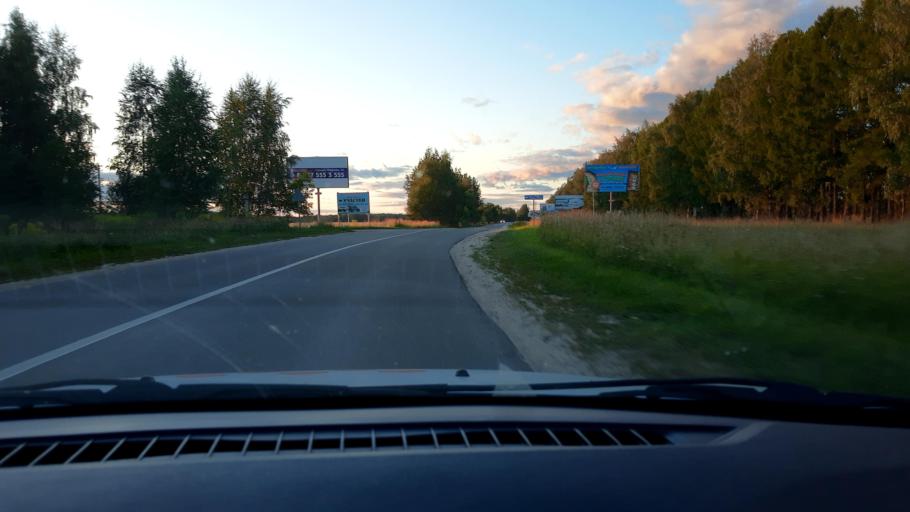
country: RU
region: Nizjnij Novgorod
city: Zavolzh'ye
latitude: 56.6931
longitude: 43.4177
